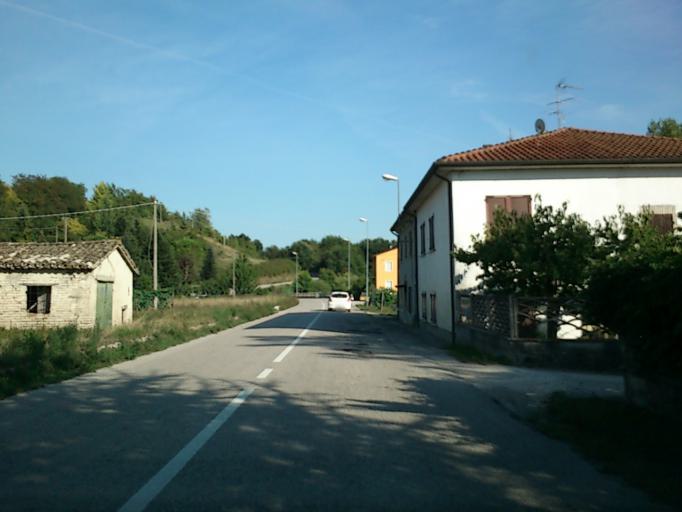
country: IT
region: The Marches
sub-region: Provincia di Pesaro e Urbino
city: Canavaccio
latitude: 43.6843
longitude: 12.7262
